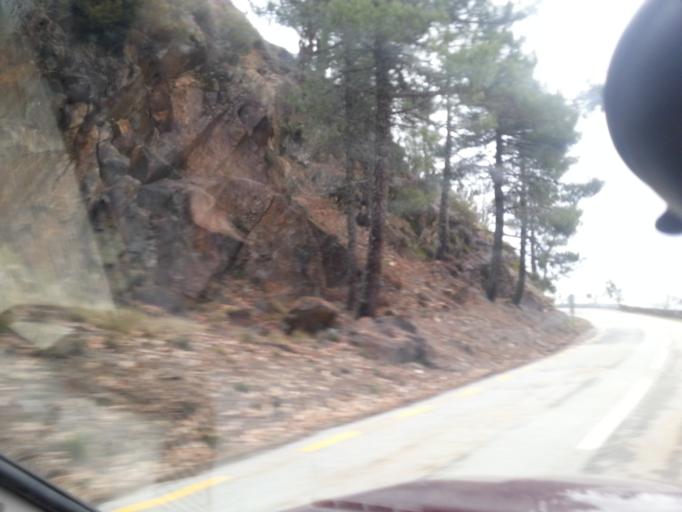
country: PT
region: Guarda
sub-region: Manteigas
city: Manteigas
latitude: 40.4126
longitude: -7.5530
